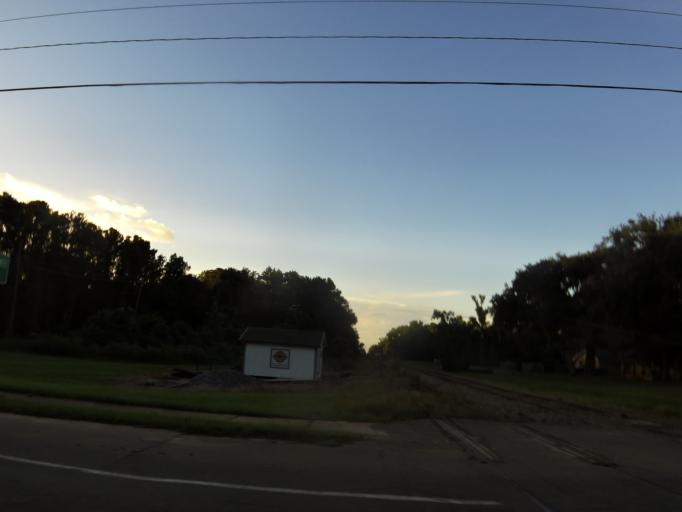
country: US
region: Georgia
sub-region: Camden County
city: Kingsland
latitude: 30.7999
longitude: -81.6913
